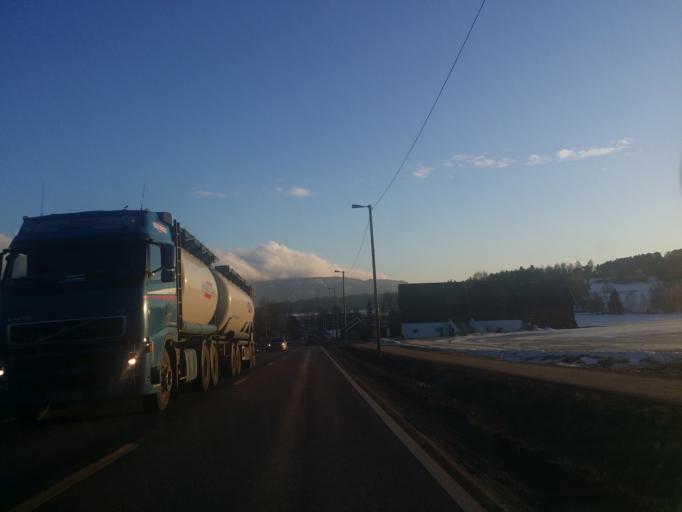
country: NO
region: Buskerud
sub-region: Hole
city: Vik
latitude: 60.1218
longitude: 10.2807
